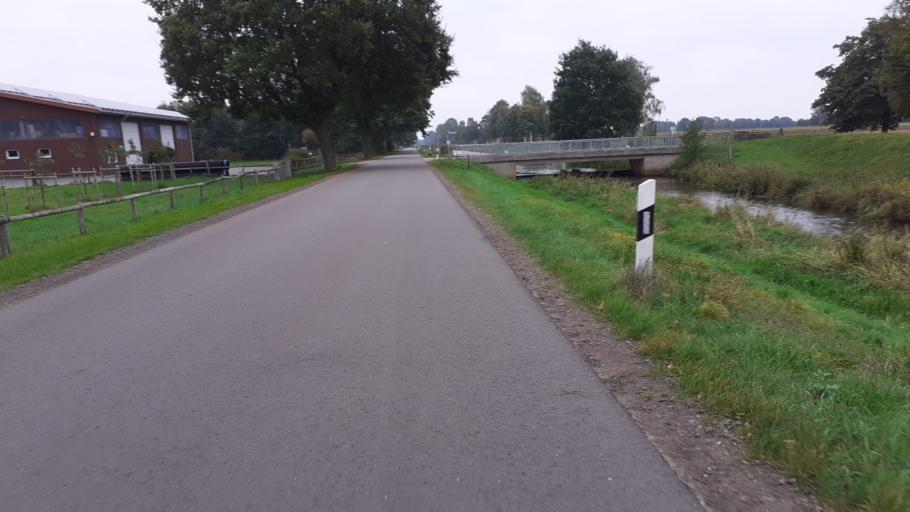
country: DE
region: Lower Saxony
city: Oldenburg
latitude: 53.1149
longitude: 8.2975
